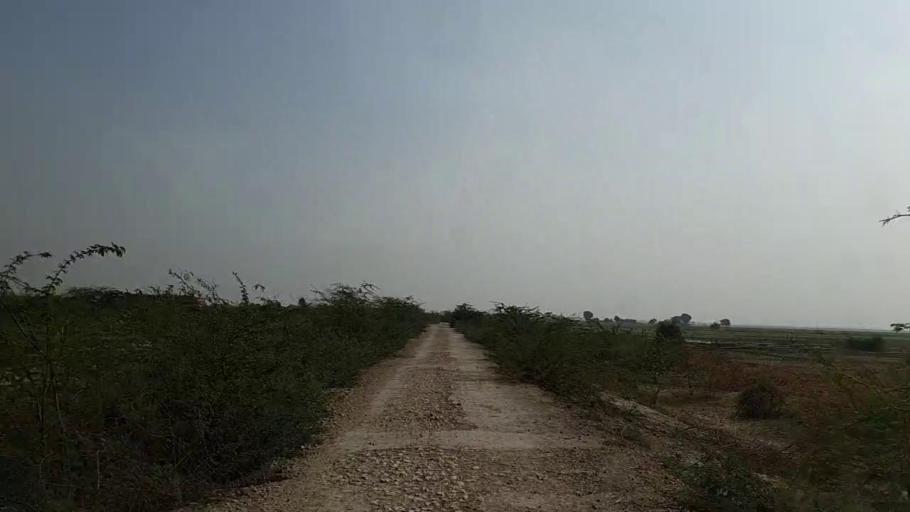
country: PK
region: Sindh
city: Naukot
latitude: 24.7571
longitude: 69.3035
